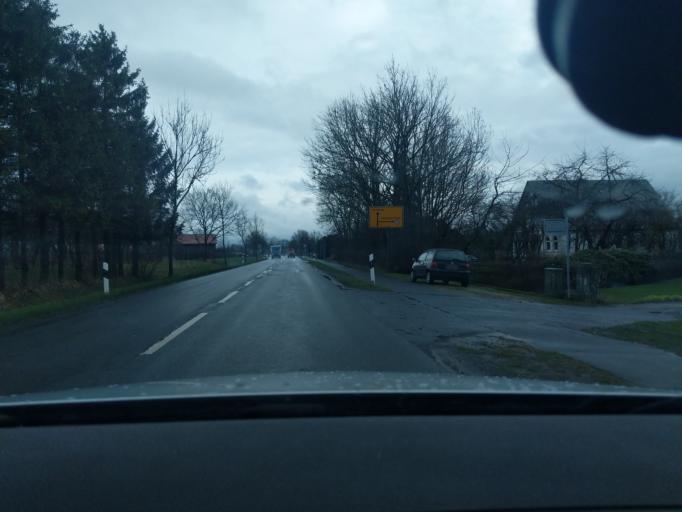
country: DE
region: Lower Saxony
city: Jork
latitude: 53.5523
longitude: 9.6630
